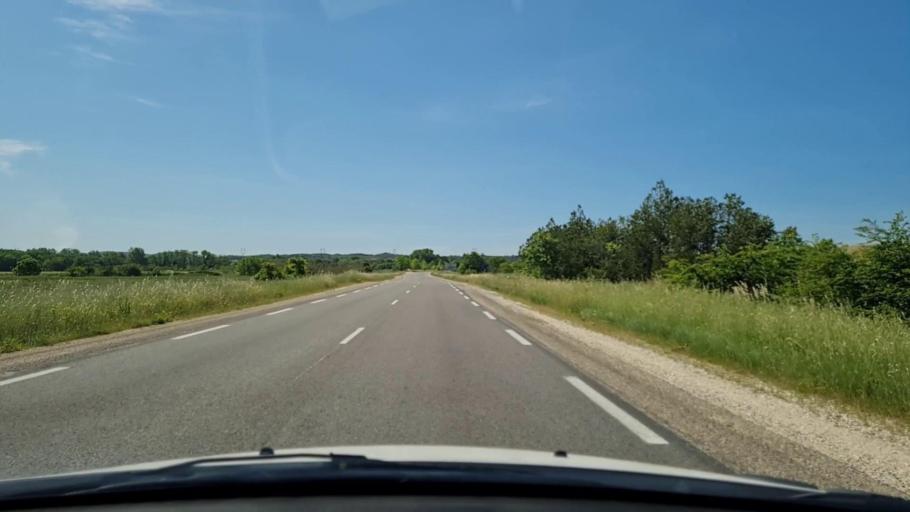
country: FR
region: Languedoc-Roussillon
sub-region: Departement du Gard
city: La Calmette
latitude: 43.9381
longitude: 4.2546
